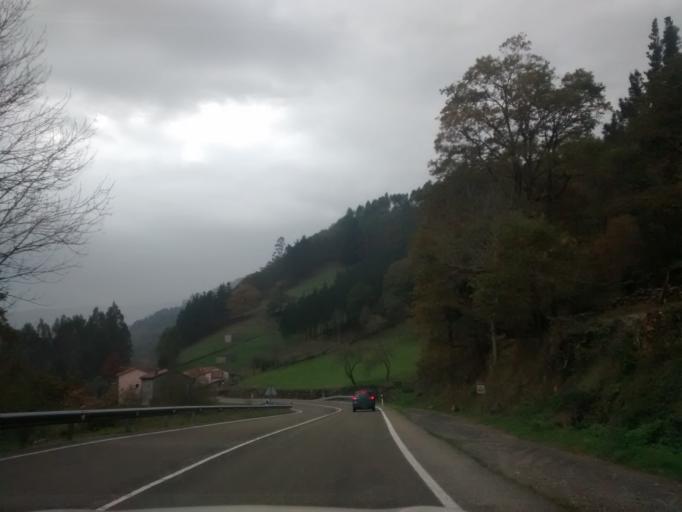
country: ES
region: Cantabria
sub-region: Provincia de Cantabria
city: San Pedro del Romeral
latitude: 43.1532
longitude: -3.8970
